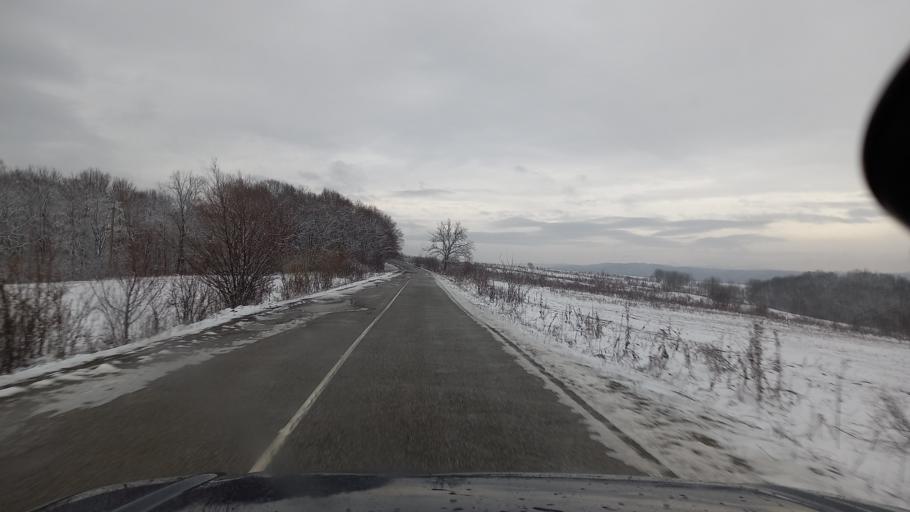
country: RU
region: Adygeya
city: Abadzekhskaya
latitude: 44.3514
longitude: 40.3661
